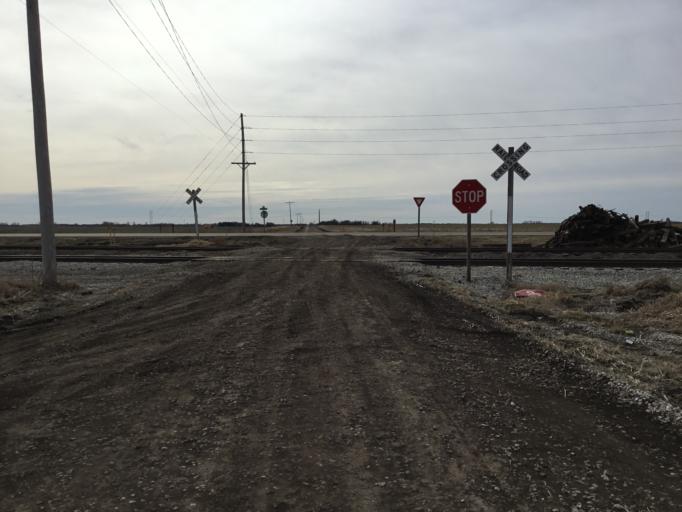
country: US
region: Kansas
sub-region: McPherson County
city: McPherson
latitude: 38.3764
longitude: -97.8141
